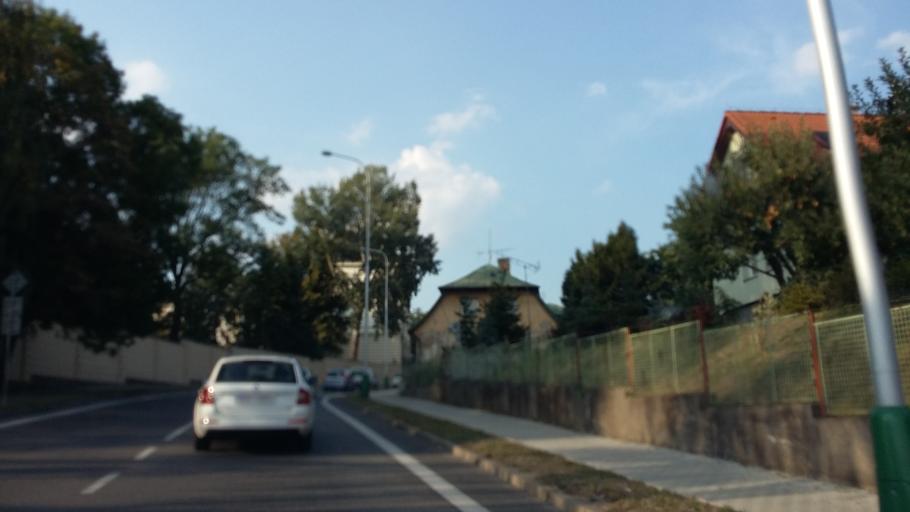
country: CZ
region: Central Bohemia
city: Kosmonosy
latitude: 50.4422
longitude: 14.9292
